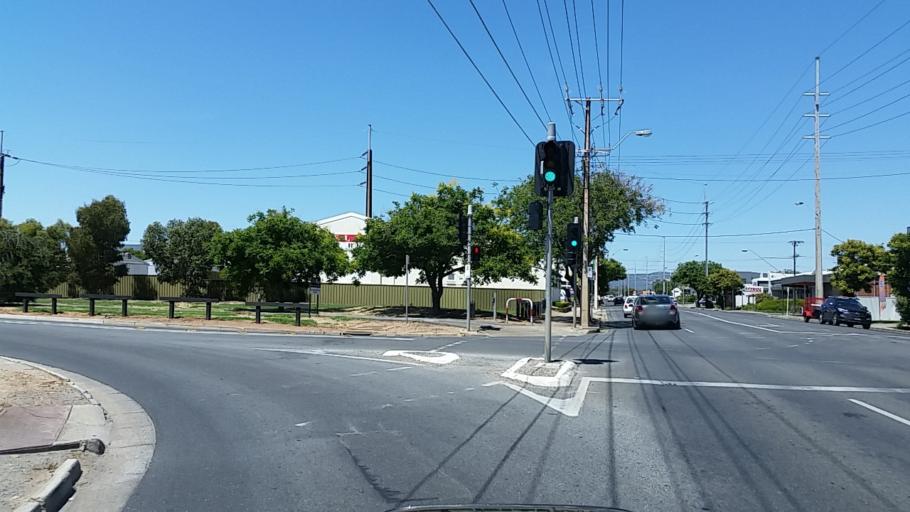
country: AU
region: South Australia
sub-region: Unley
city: Forestville
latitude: -34.9422
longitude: 138.5675
